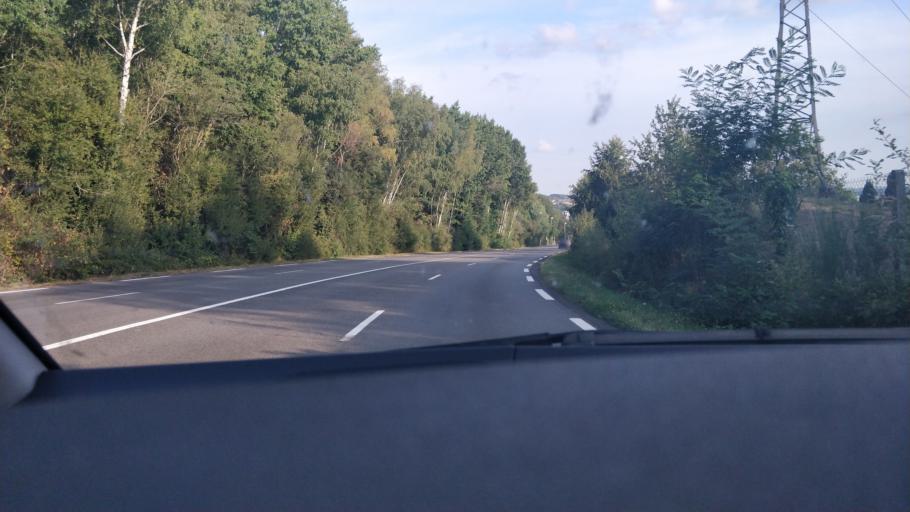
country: FR
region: Limousin
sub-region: Departement de la Haute-Vienne
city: Le Palais-sur-Vienne
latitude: 45.8546
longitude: 1.2945
